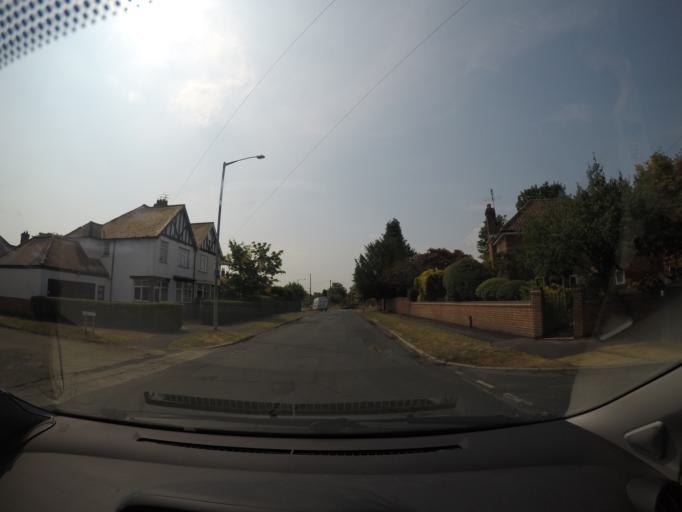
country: GB
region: England
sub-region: City of York
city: York
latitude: 53.9527
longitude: -1.1184
